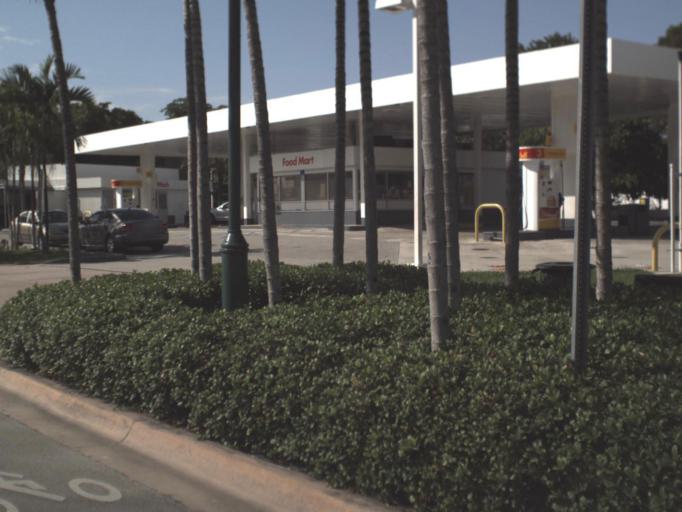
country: US
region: Florida
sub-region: Miami-Dade County
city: Key Biscayne
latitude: 25.6992
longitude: -80.1624
